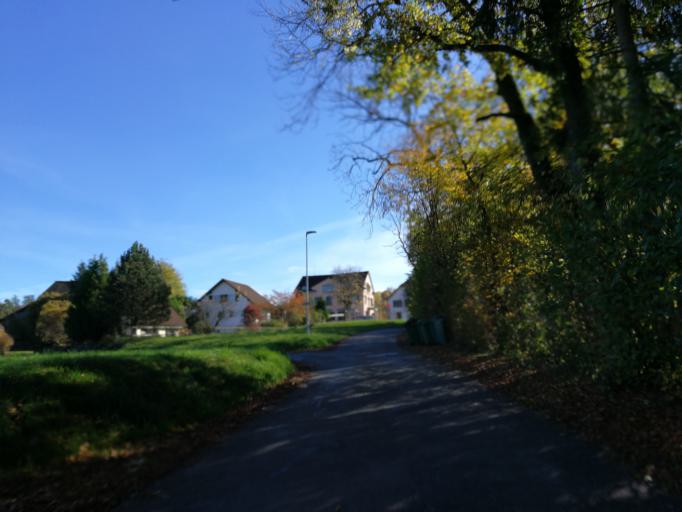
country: CH
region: Zurich
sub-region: Bezirk Meilen
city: Hombrechtikon
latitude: 47.2421
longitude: 8.7864
